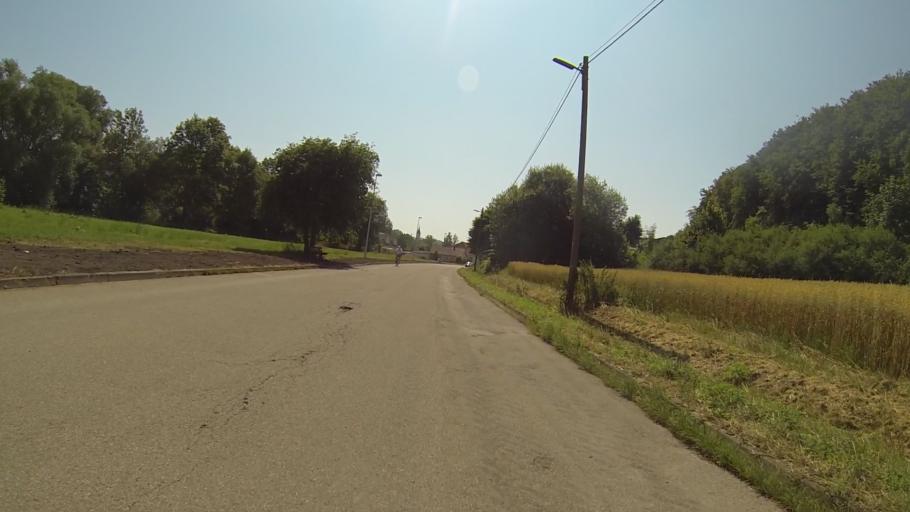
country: DE
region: Baden-Wuerttemberg
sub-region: Regierungsbezirk Stuttgart
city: Heidenheim an der Brenz
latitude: 48.7128
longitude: 10.1566
